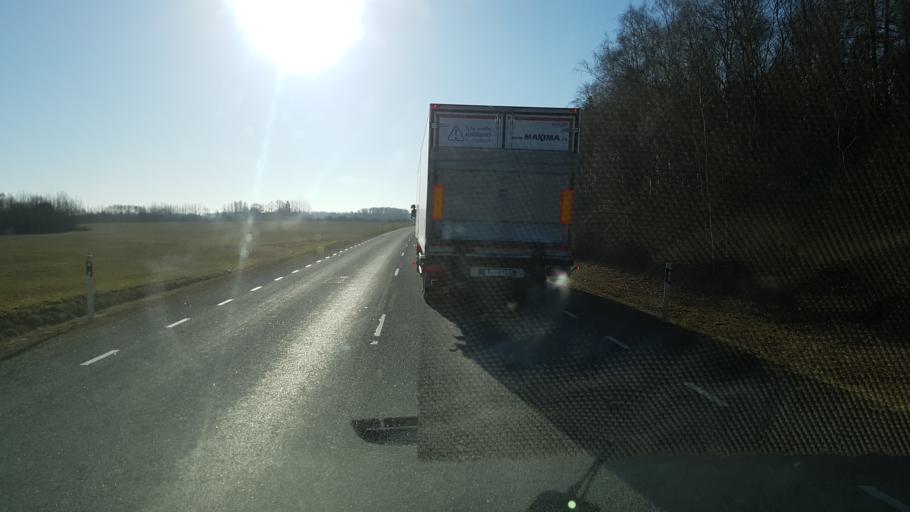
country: EE
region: Jaervamaa
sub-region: Tueri vald
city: Sarevere
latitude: 58.7782
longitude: 25.4972
